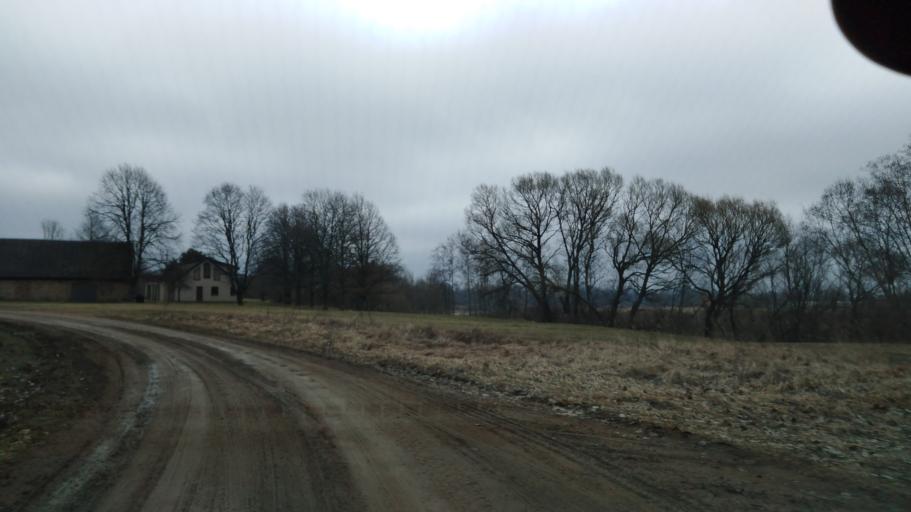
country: LV
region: Kuldigas Rajons
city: Kuldiga
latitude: 56.9836
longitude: 21.9637
